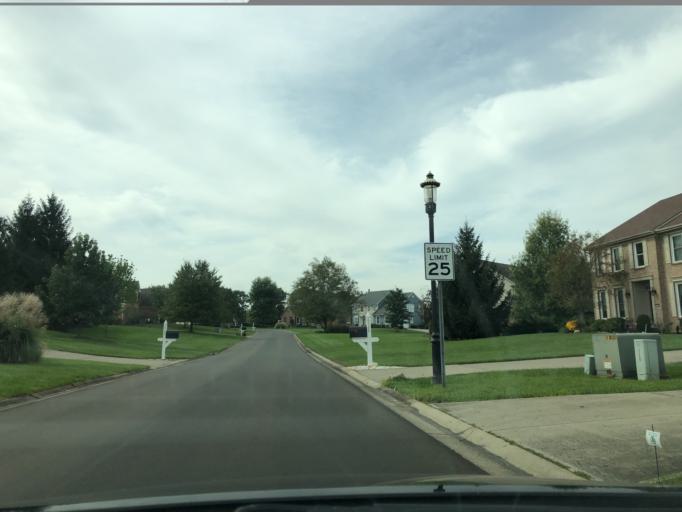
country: US
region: Ohio
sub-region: Hamilton County
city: Loveland
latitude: 39.2498
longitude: -84.2561
